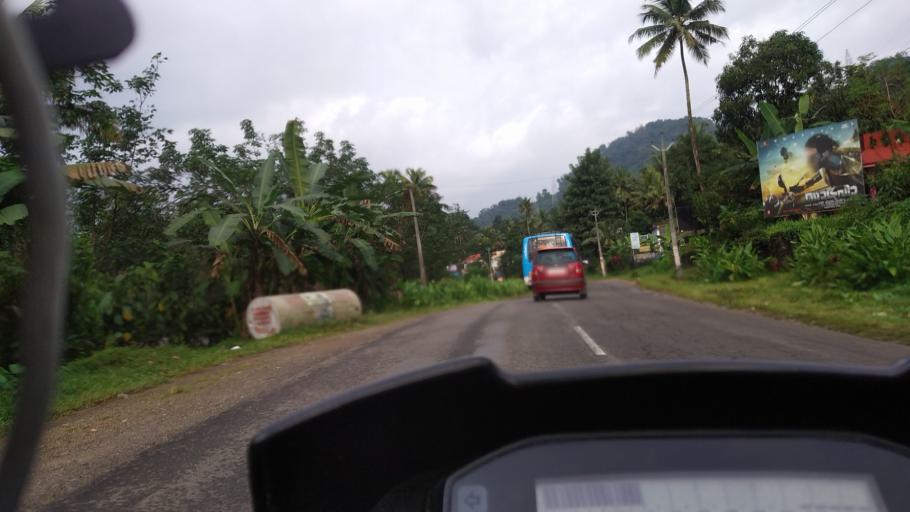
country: IN
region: Kerala
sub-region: Idukki
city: Kuttampuzha
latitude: 10.0504
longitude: 76.7524
